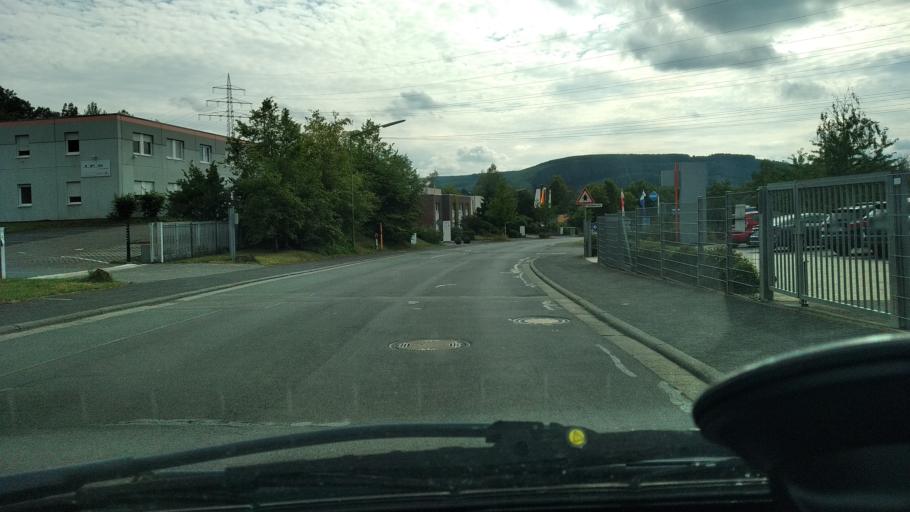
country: DE
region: North Rhine-Westphalia
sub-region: Regierungsbezirk Arnsberg
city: Burbach
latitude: 50.7509
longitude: 8.1021
